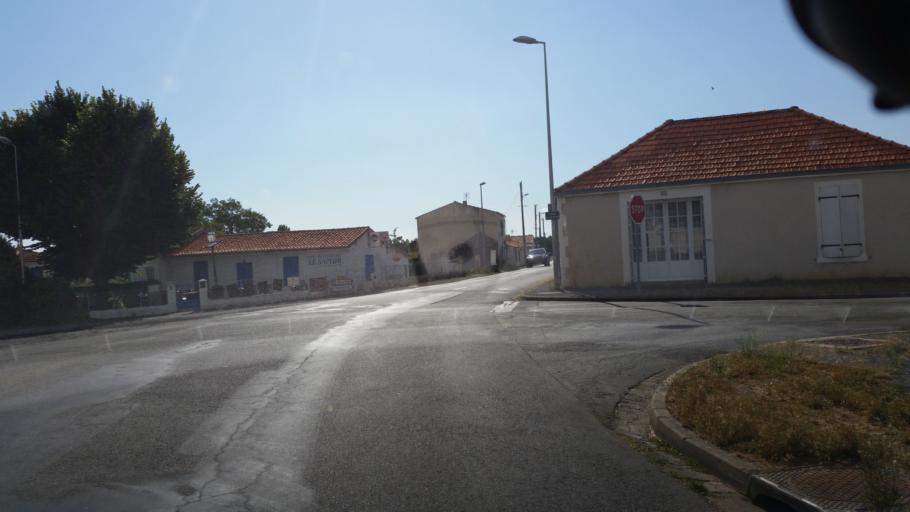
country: FR
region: Poitou-Charentes
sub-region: Departement de la Charente-Maritime
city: Marans
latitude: 46.3049
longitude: -1.0006
